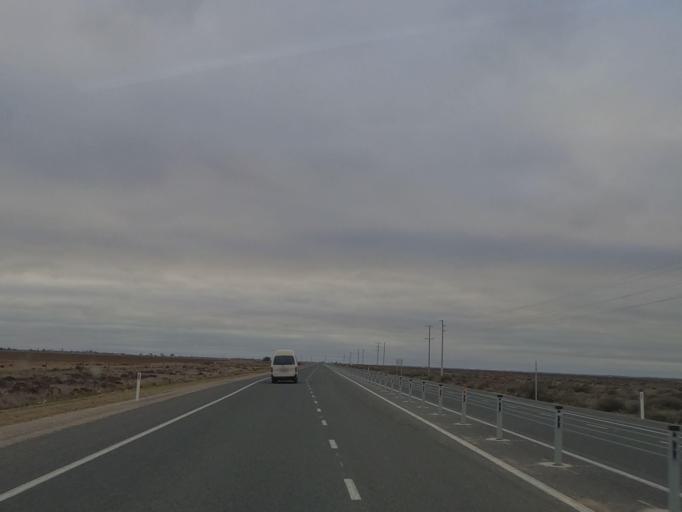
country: AU
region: Victoria
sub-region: Swan Hill
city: Swan Hill
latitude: -35.5161
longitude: 143.7281
